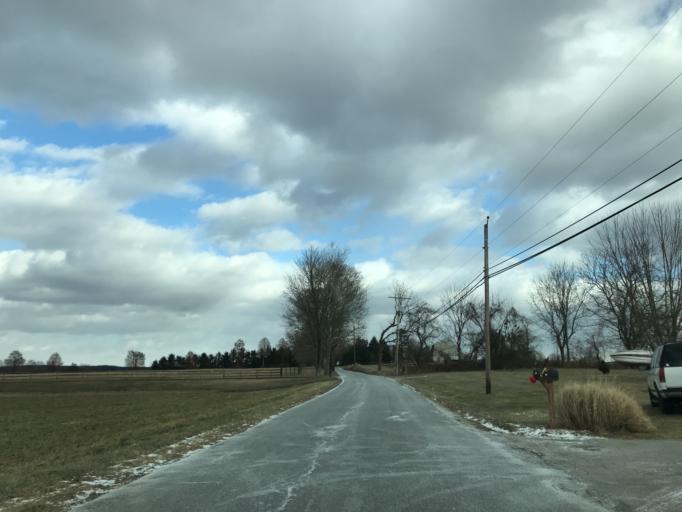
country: US
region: Maryland
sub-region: Harford County
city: Jarrettsville
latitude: 39.5747
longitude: -76.5686
